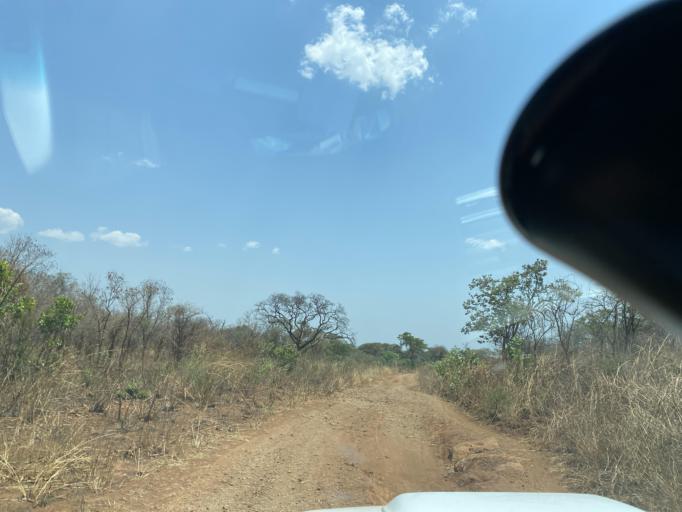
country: ZM
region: Lusaka
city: Lusaka
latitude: -15.5075
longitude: 28.0069
